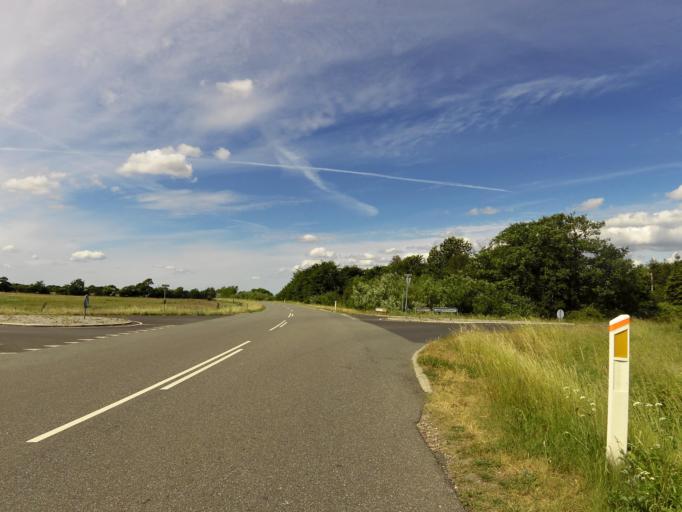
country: DK
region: South Denmark
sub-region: Esbjerg Kommune
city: Ribe
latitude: 55.3135
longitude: 8.7604
